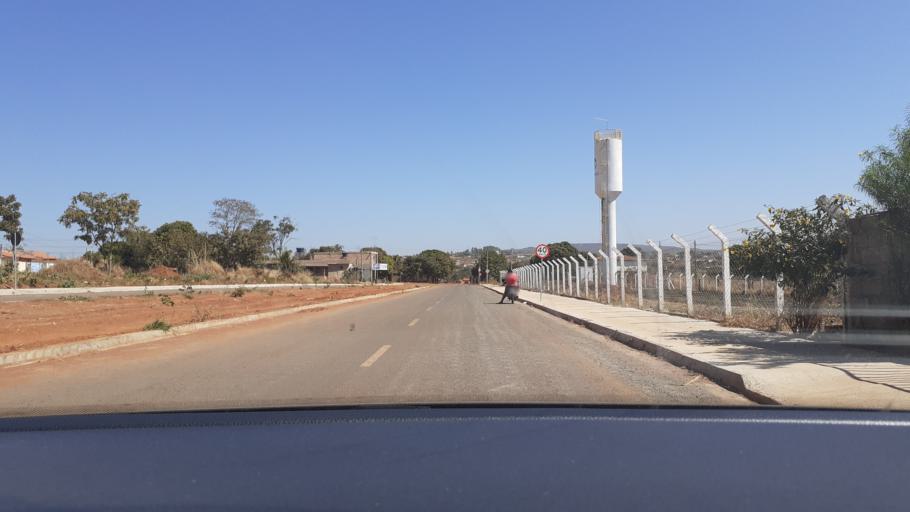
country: BR
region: Goias
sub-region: Aparecida De Goiania
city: Aparecida de Goiania
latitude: -16.8794
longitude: -49.2555
